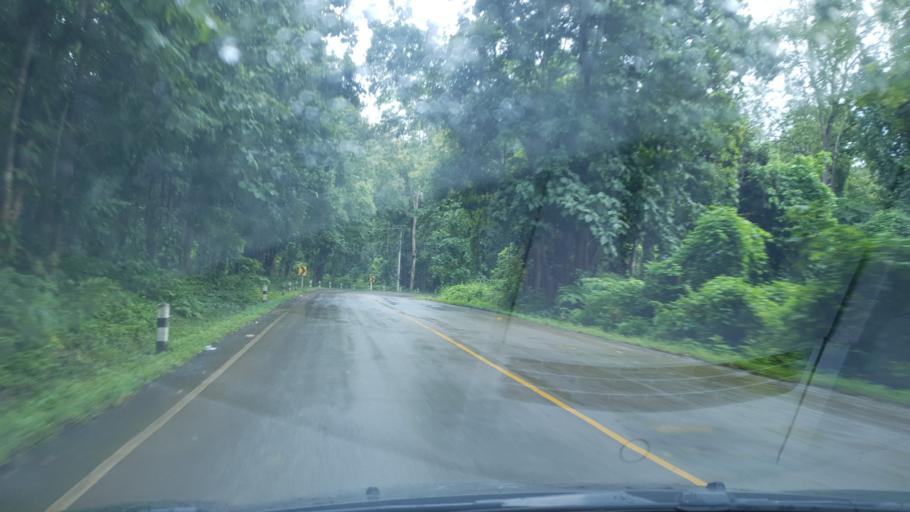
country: TH
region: Mae Hong Son
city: Pa Pae
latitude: 18.2519
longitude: 97.9428
